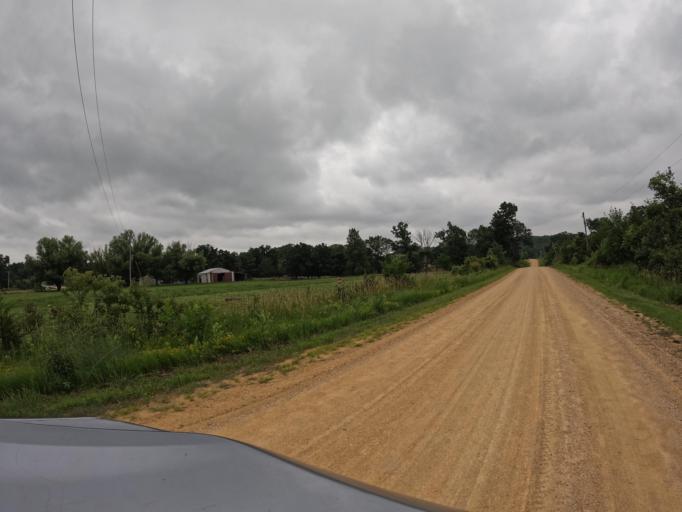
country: US
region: Illinois
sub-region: Carroll County
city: Savanna
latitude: 41.9966
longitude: -90.1843
